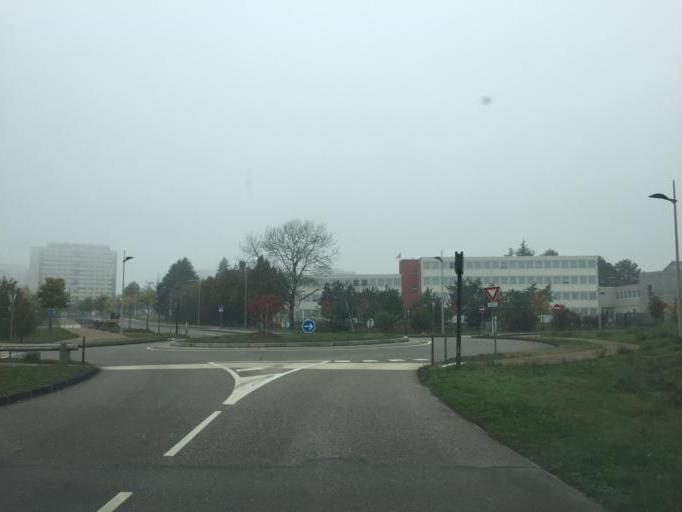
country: FR
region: Rhone-Alpes
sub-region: Departement du Rhone
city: Rillieux-la-Pape
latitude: 45.8203
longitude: 4.9125
